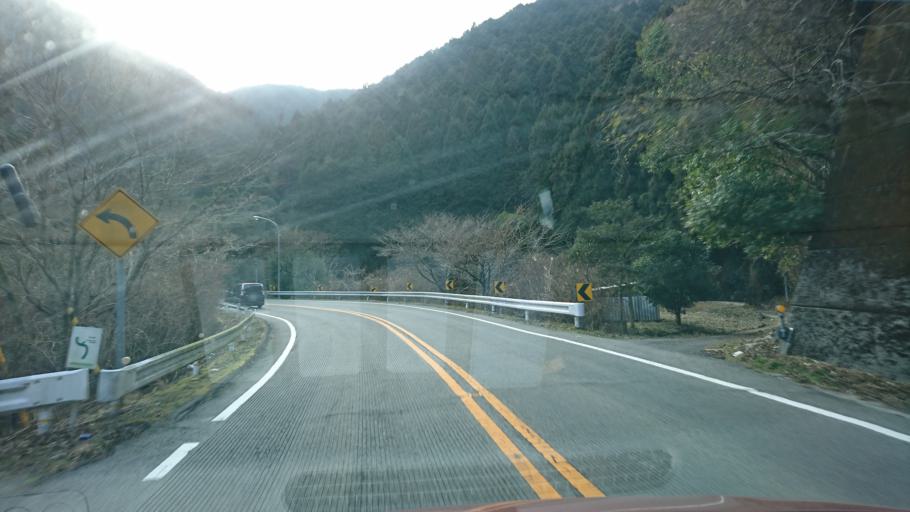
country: JP
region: Ehime
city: Hojo
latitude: 33.9573
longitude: 132.9092
